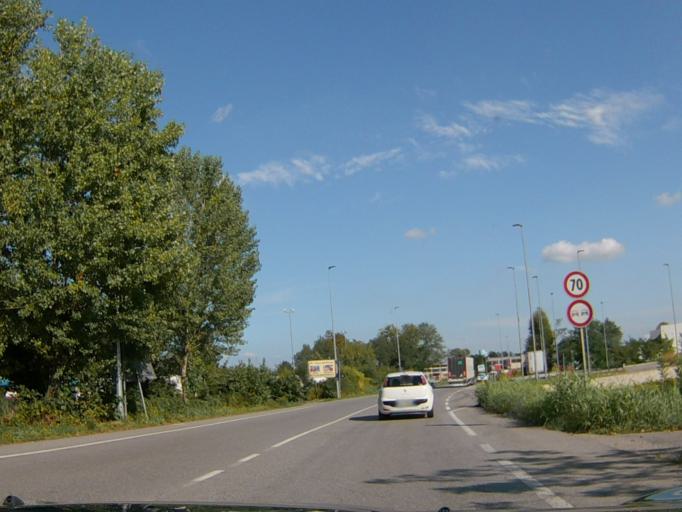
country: IT
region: Lombardy
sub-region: Provincia di Bergamo
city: Telgate
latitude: 45.6372
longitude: 9.8544
